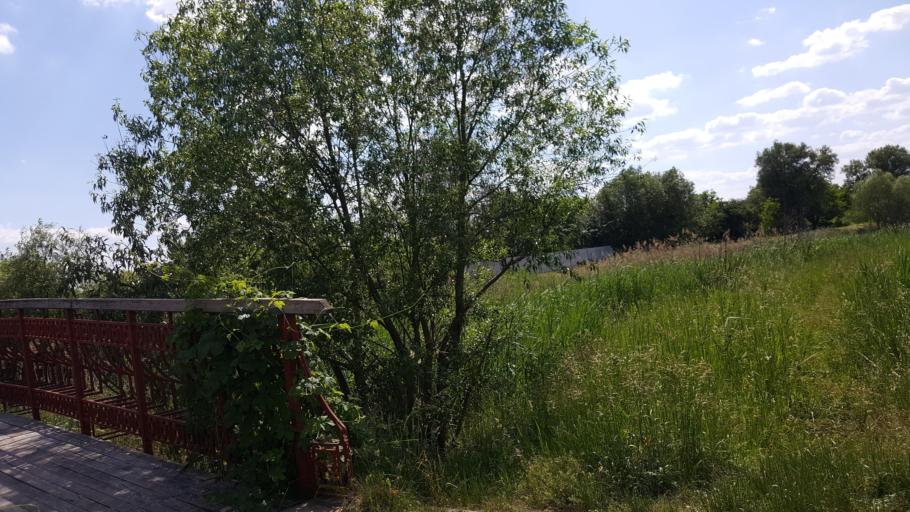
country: BY
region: Brest
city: Kobryn
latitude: 52.2160
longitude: 24.3538
